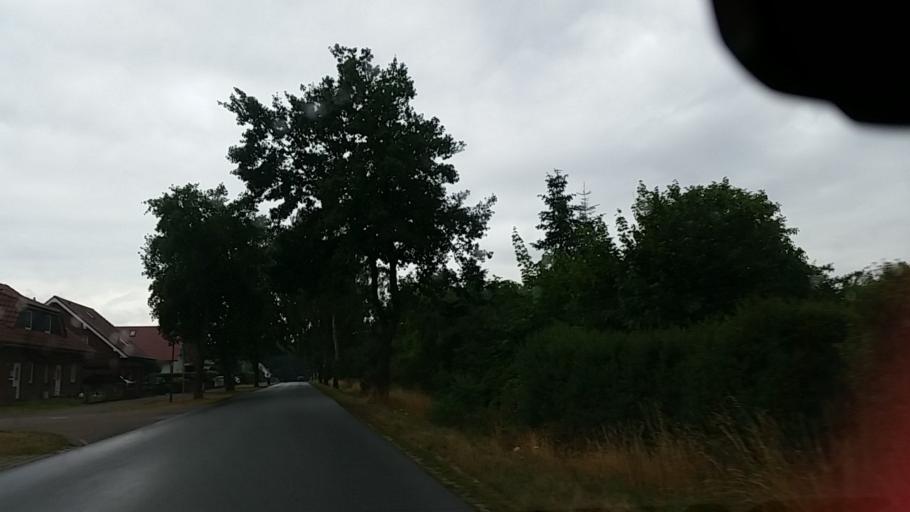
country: DE
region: Lower Saxony
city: Bokensdorf
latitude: 52.5045
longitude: 10.7161
